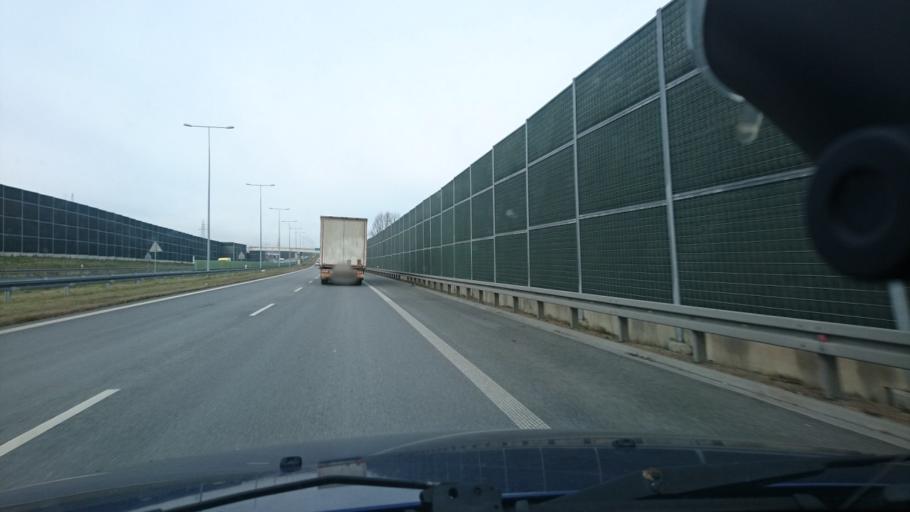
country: PL
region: Silesian Voivodeship
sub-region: Powiat bielski
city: Wilkowice
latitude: 49.7582
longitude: 19.0865
